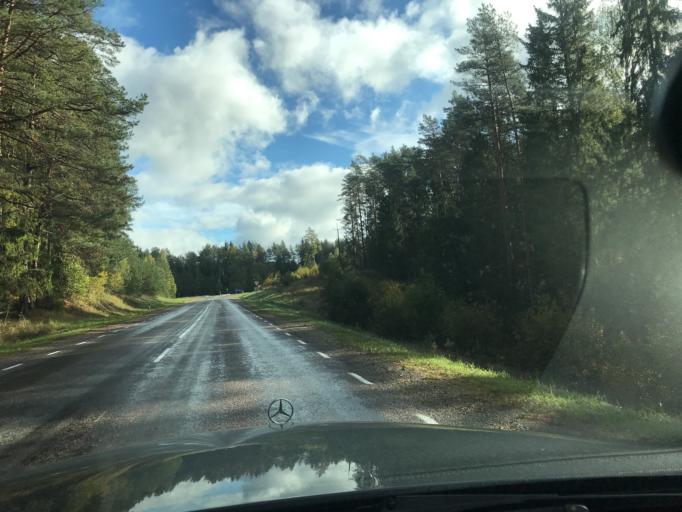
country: EE
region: Valgamaa
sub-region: Torva linn
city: Torva
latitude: 58.0095
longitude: 26.1576
